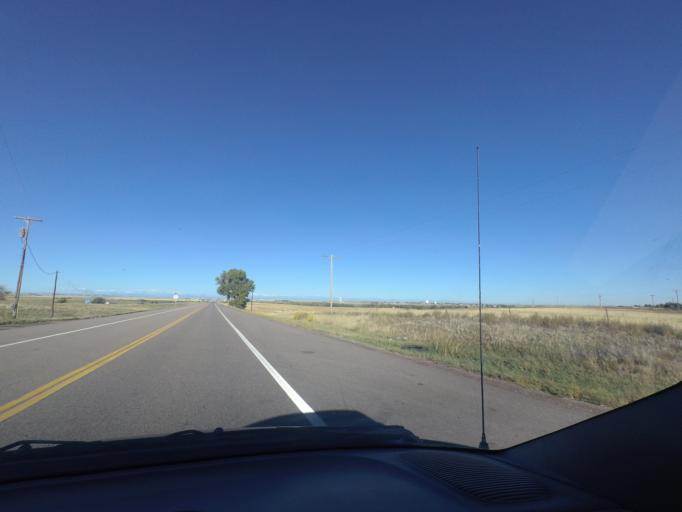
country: US
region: Colorado
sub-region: Adams County
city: Bennett
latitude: 39.7381
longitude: -104.3993
